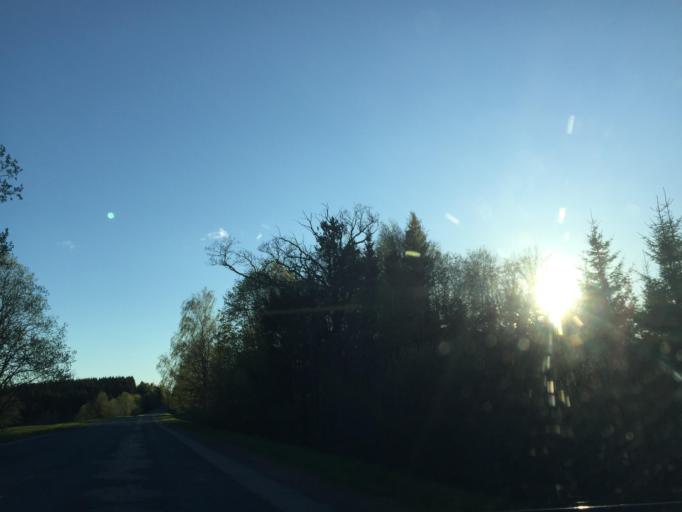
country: LV
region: Ergli
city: Ergli
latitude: 56.8783
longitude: 25.7254
